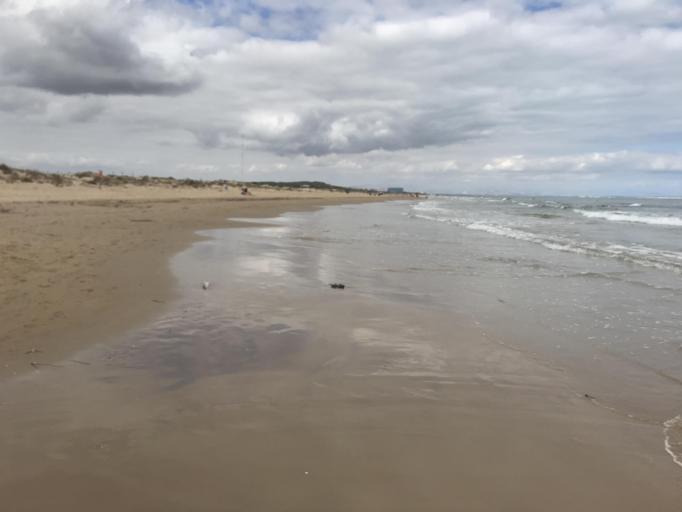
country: ES
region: Valencia
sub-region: Provincia de Alicante
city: Guardamar del Segura
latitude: 38.0336
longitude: -0.6517
